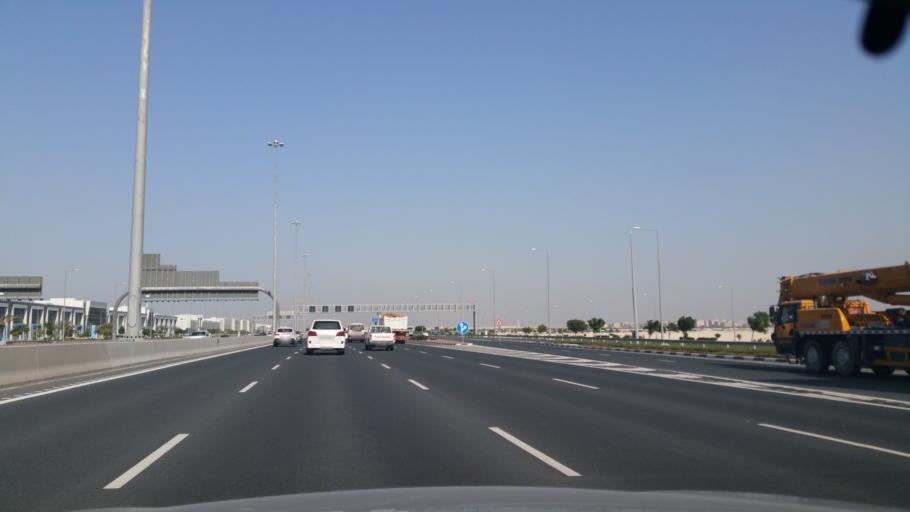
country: QA
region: Al Wakrah
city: Al Wukayr
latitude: 25.1980
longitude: 51.4688
